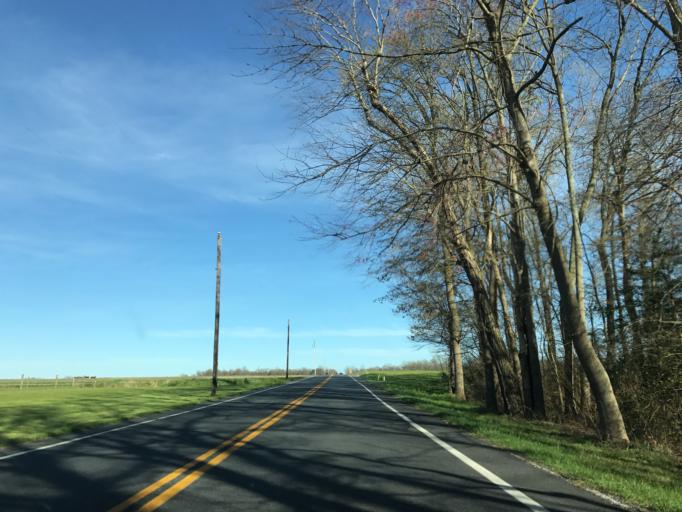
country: US
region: Maryland
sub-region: Caroline County
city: Greensboro
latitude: 39.0341
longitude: -75.7719
